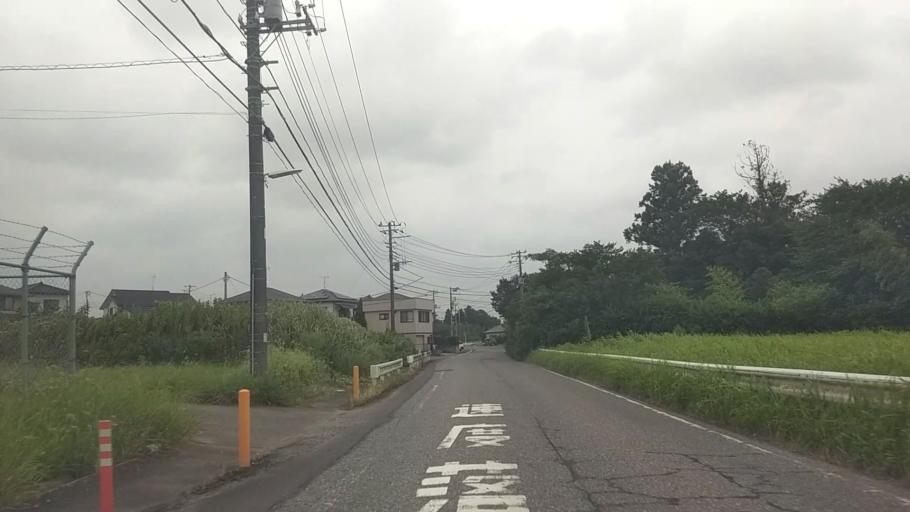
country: JP
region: Chiba
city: Kisarazu
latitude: 35.3747
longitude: 140.0134
